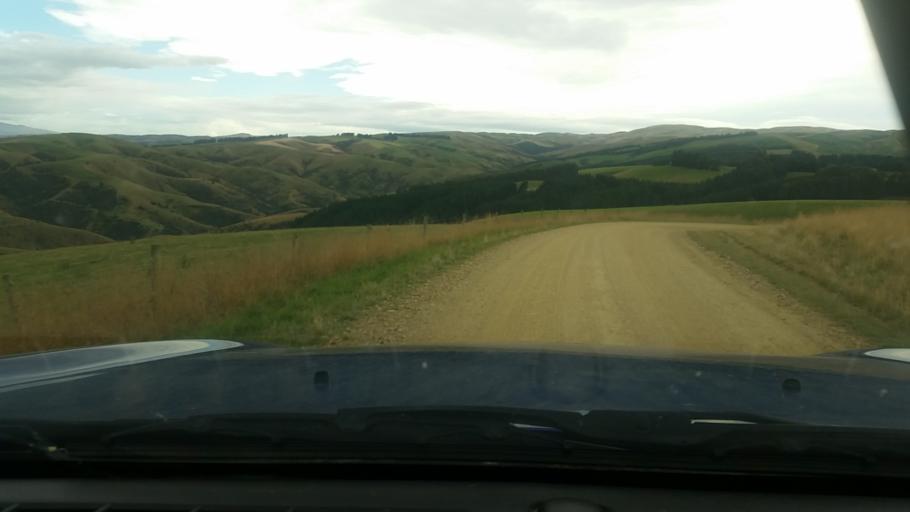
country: NZ
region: Otago
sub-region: Clutha District
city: Balclutha
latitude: -45.6832
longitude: 169.4918
